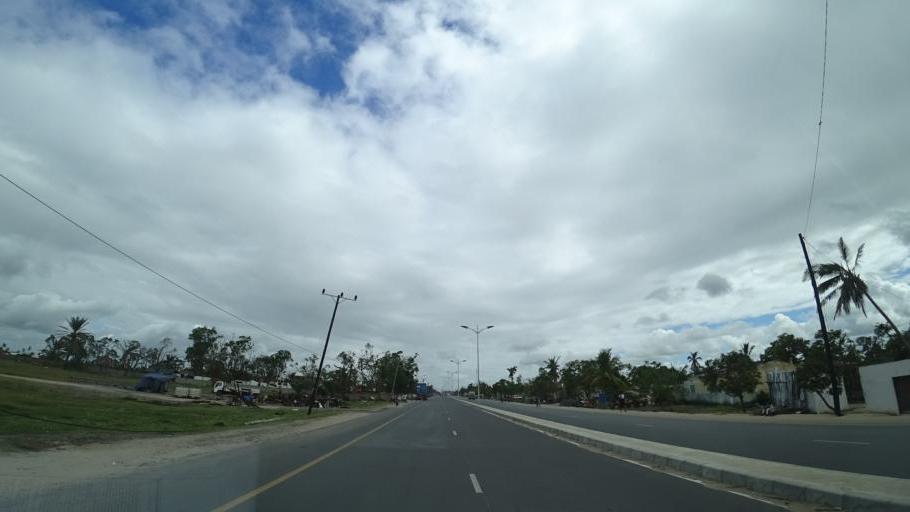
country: MZ
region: Sofala
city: Beira
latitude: -19.7276
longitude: 34.8180
